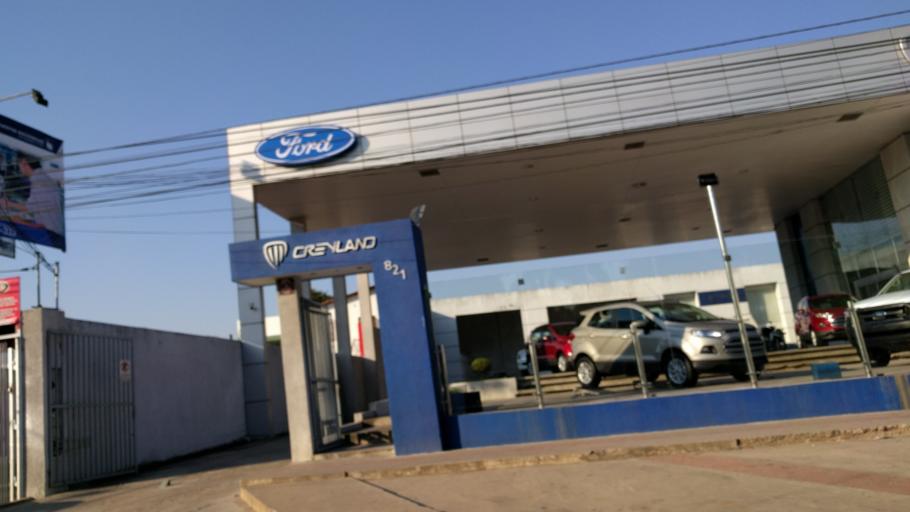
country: BO
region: Santa Cruz
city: Santa Cruz de la Sierra
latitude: -17.7734
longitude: -63.1935
